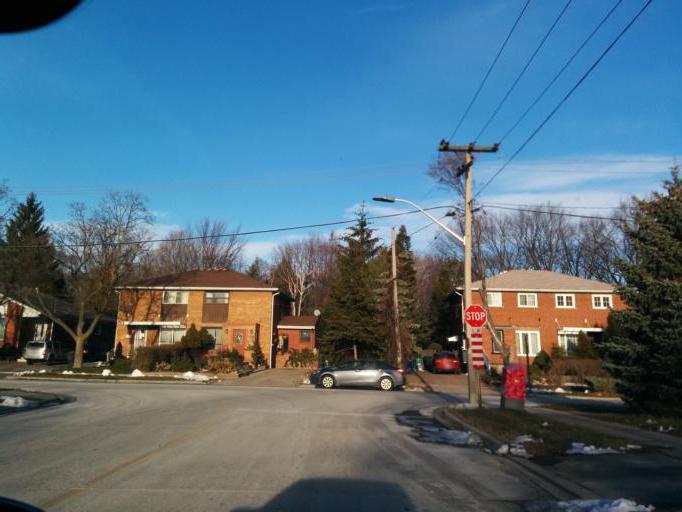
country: CA
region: Ontario
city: Etobicoke
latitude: 43.6103
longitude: -79.5953
